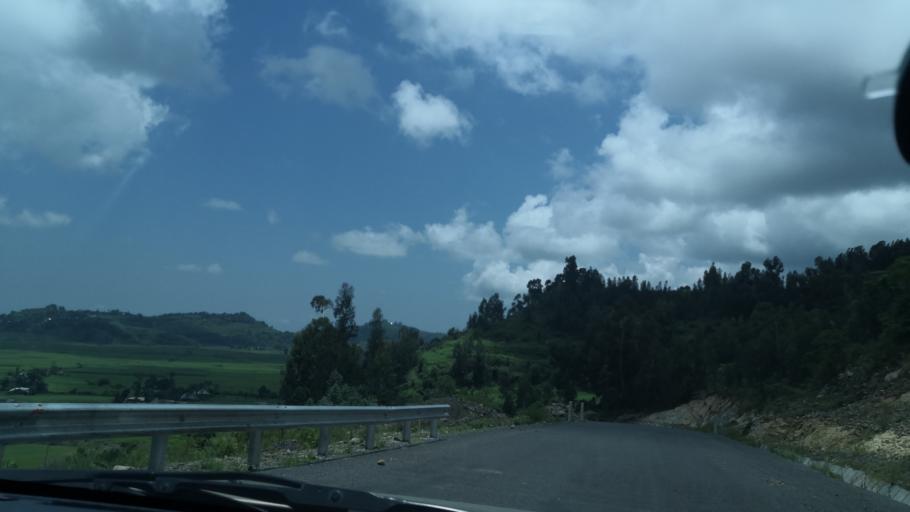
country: ET
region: Amhara
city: Abomsa
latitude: 10.3317
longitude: 39.8543
